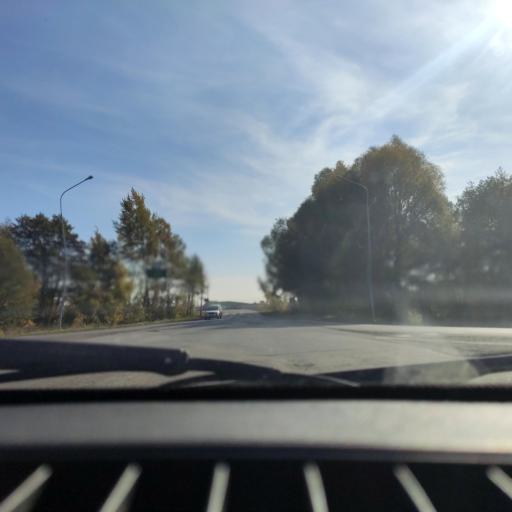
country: RU
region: Bashkortostan
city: Avdon
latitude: 54.6625
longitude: 55.7357
